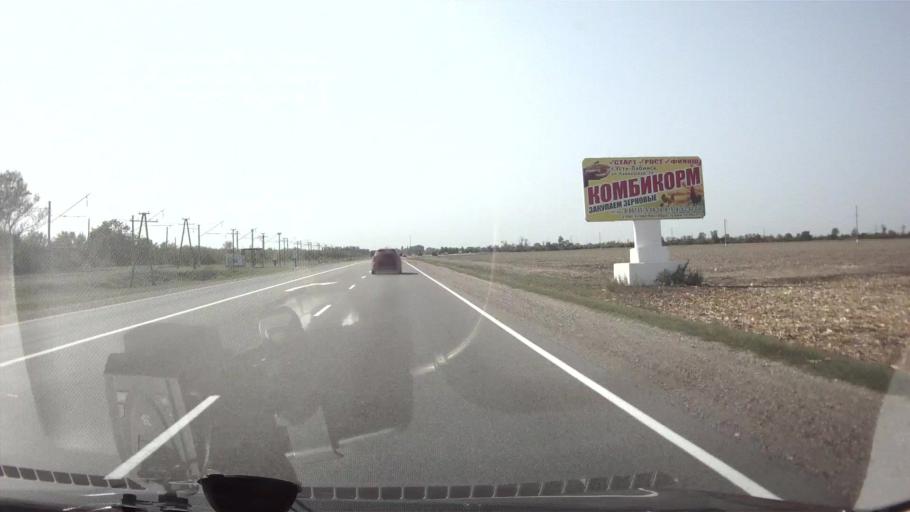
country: RU
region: Krasnodarskiy
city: Dvubratskiy
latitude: 45.2467
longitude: 39.7538
